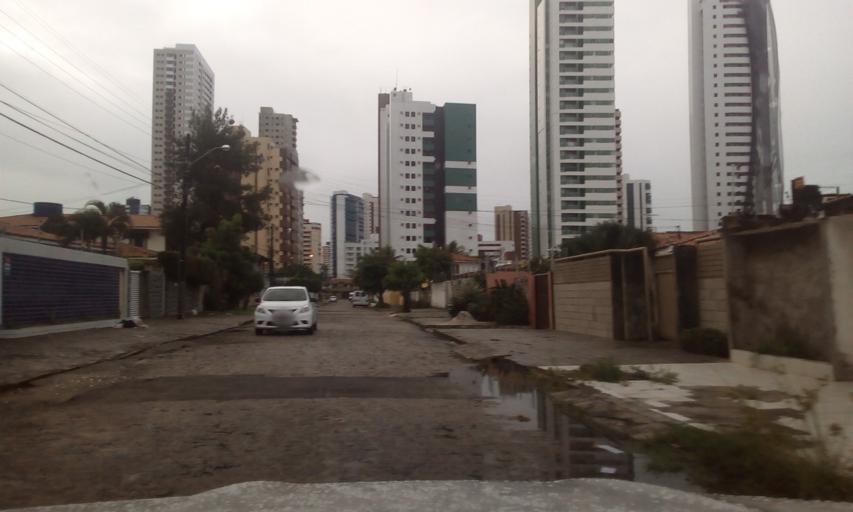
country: BR
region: Paraiba
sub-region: Joao Pessoa
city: Joao Pessoa
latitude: -7.1034
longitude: -34.8401
